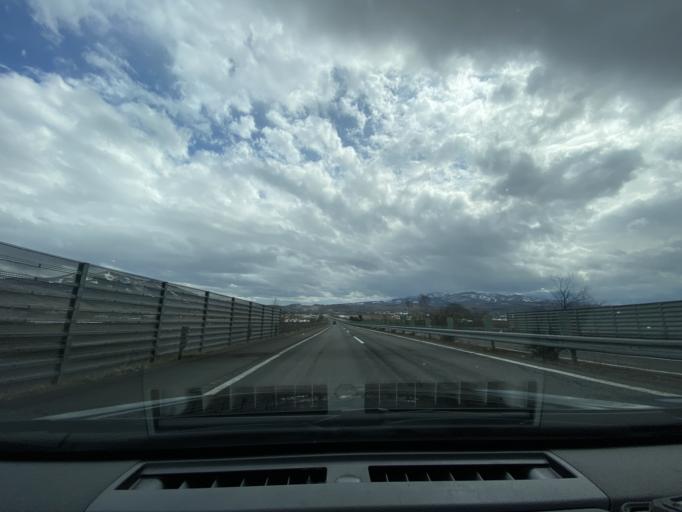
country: JP
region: Hokkaido
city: Fukagawa
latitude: 43.7389
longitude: 142.1649
